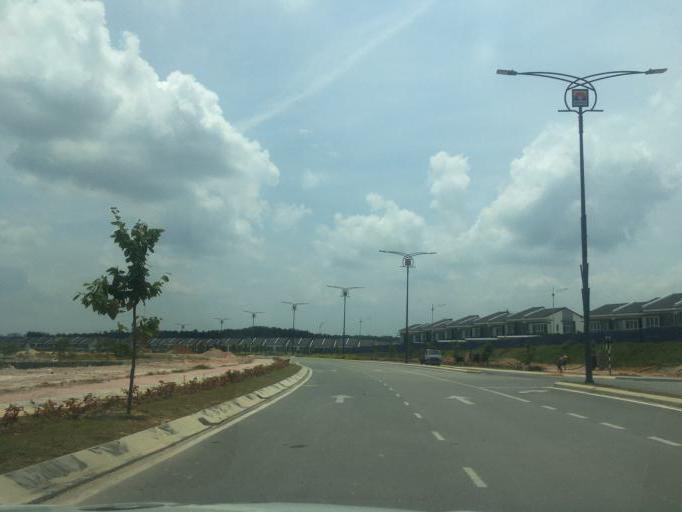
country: MY
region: Putrajaya
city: Putrajaya
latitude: 2.8541
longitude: 101.7054
